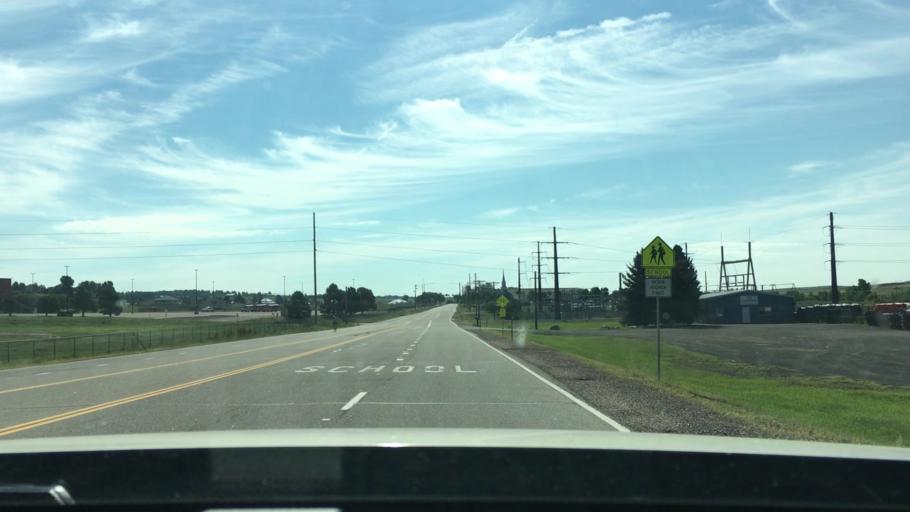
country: US
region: Colorado
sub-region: Douglas County
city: The Pinery
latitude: 39.4348
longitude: -104.7591
